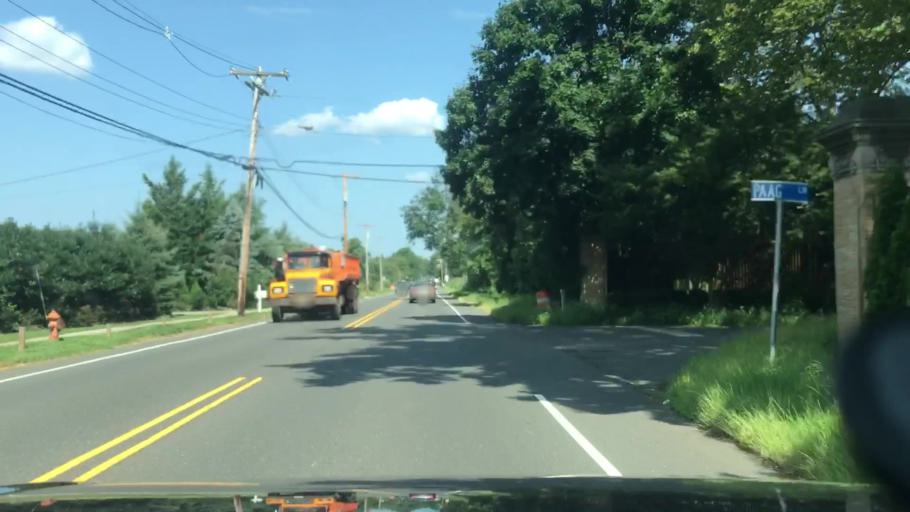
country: US
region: New Jersey
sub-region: Monmouth County
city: Oceanport
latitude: 40.3301
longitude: -74.0240
